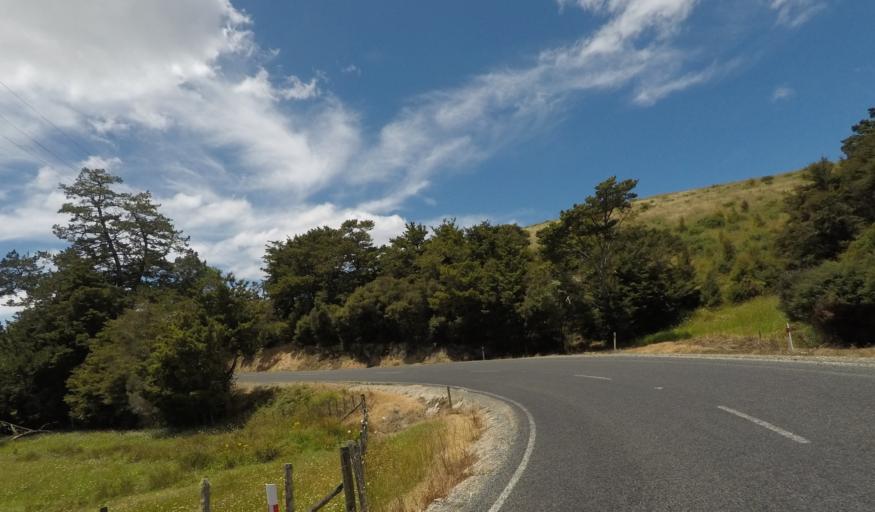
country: NZ
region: Northland
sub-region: Whangarei
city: Ngunguru
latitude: -35.5068
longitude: 174.4235
